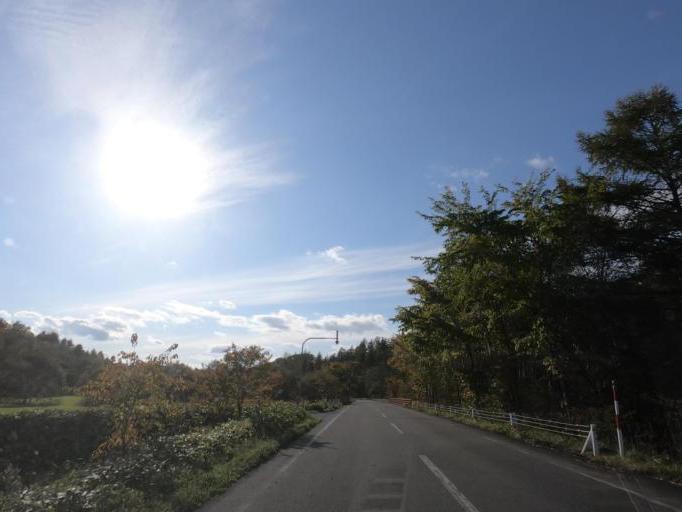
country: JP
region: Hokkaido
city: Obihiro
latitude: 42.6160
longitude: 143.3961
